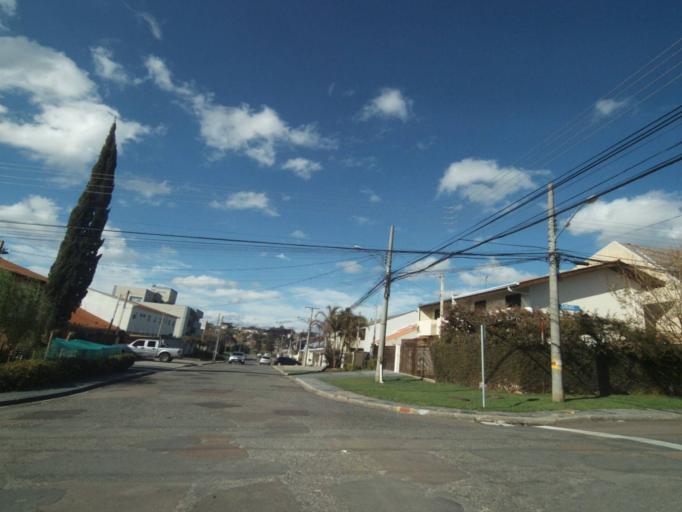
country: BR
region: Parana
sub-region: Curitiba
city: Curitiba
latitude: -25.3853
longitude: -49.2499
